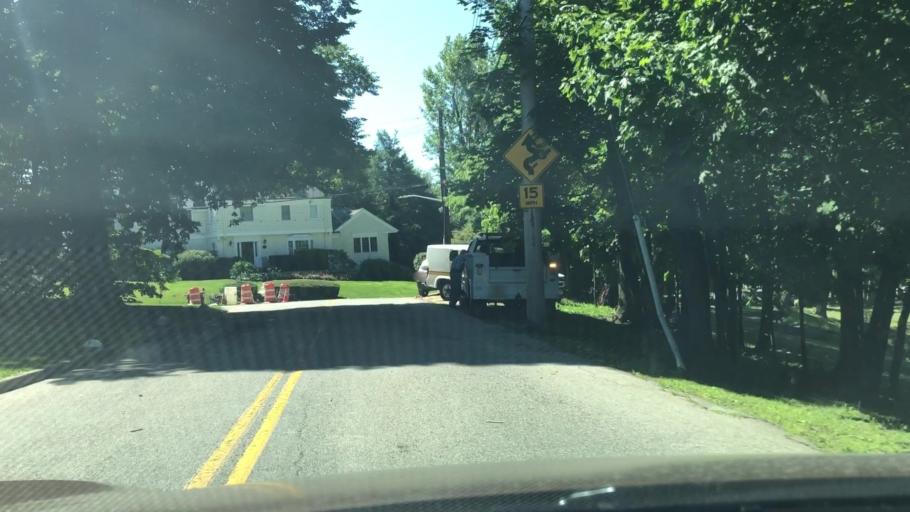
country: US
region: New York
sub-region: Westchester County
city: White Plains
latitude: 41.0179
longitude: -73.7469
